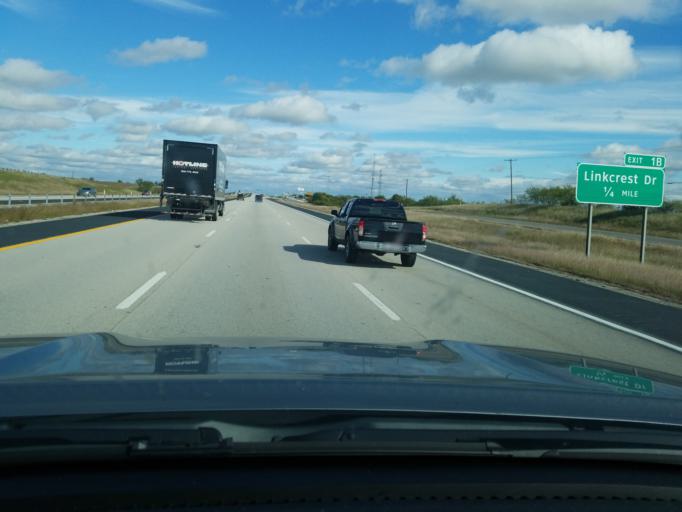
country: US
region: Texas
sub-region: Parker County
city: Aledo
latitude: 32.7208
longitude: -97.5451
